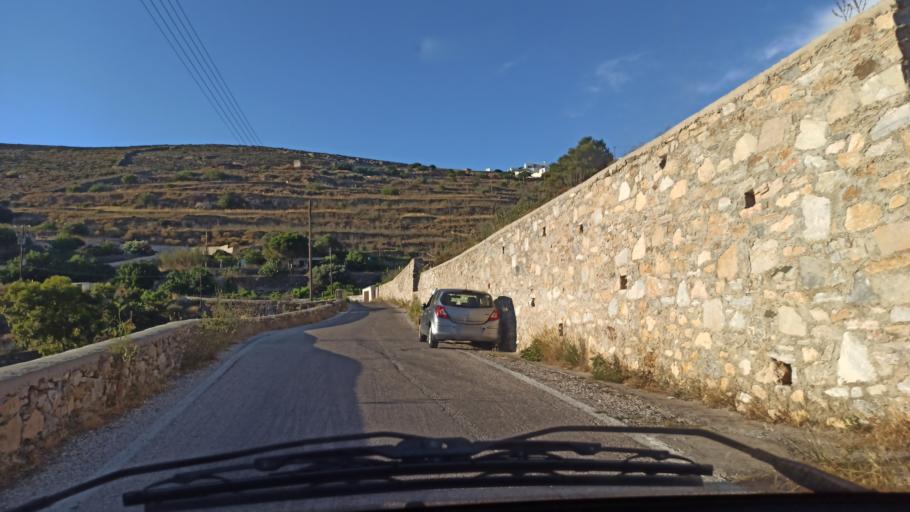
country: GR
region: South Aegean
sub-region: Nomos Kykladon
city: Ano Syros
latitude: 37.4620
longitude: 24.9327
